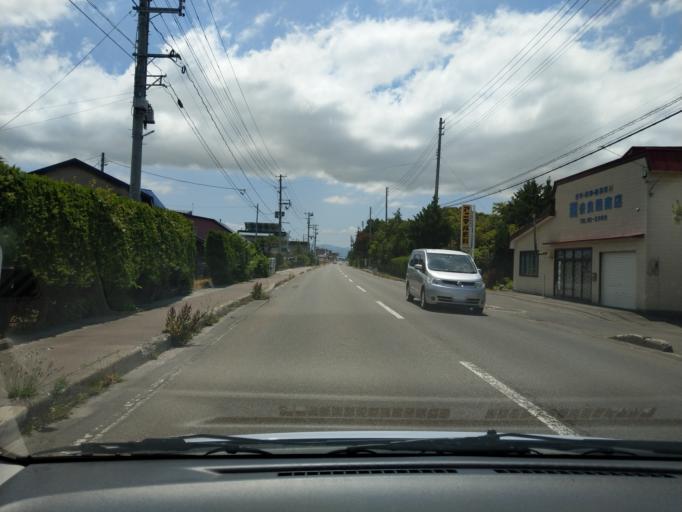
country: JP
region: Aomori
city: Namioka
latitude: 40.6876
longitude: 140.5567
